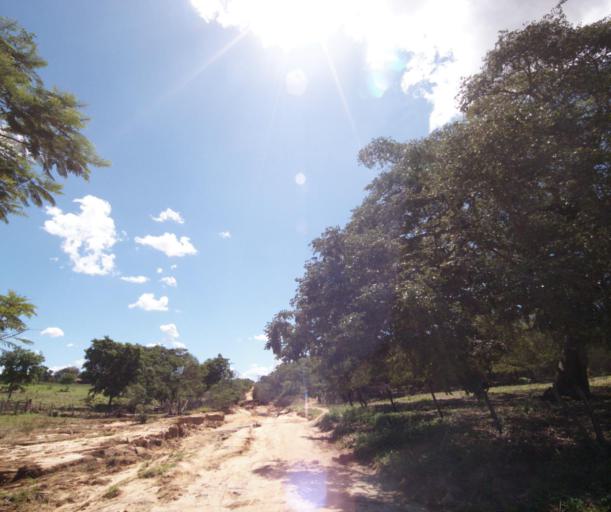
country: BR
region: Bahia
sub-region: Carinhanha
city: Carinhanha
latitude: -14.2362
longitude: -44.3192
